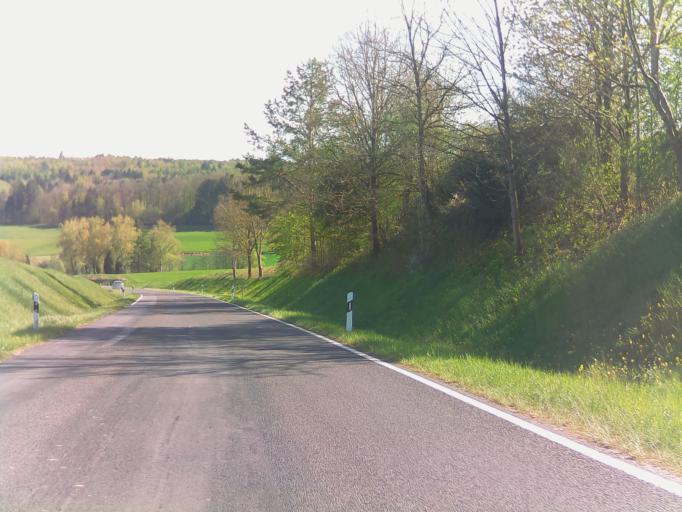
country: DE
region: Bavaria
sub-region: Regierungsbezirk Unterfranken
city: Burgpreppach
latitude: 50.1080
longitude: 10.6429
